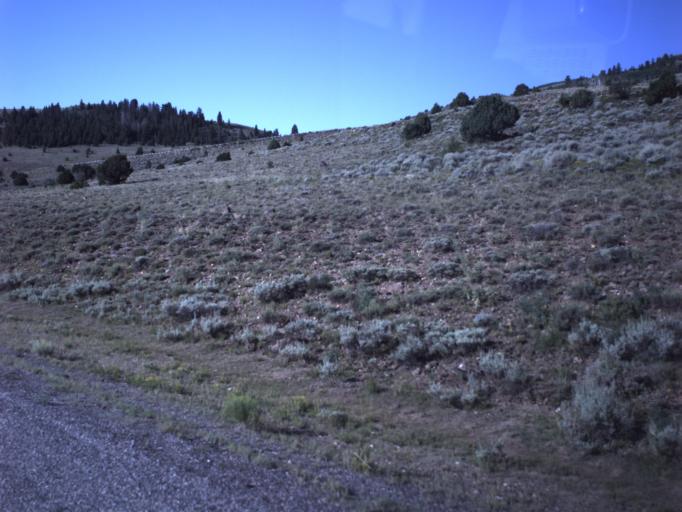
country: US
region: Utah
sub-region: Wayne County
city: Loa
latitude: 38.6051
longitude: -111.4622
